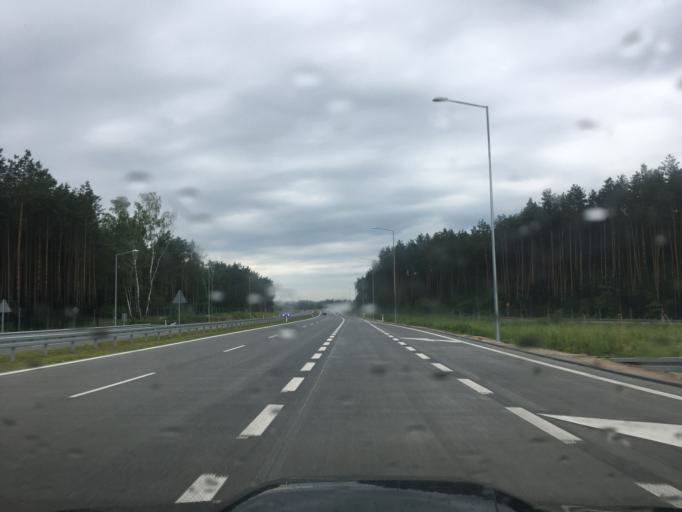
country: PL
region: Masovian Voivodeship
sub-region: Powiat piaseczynski
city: Gora Kalwaria
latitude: 51.9722
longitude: 21.1934
